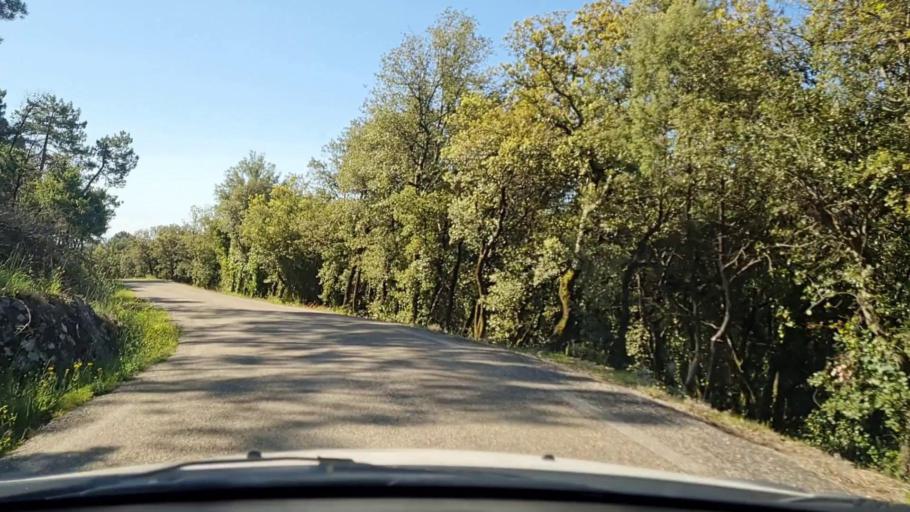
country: FR
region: Languedoc-Roussillon
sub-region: Departement du Gard
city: Branoux-les-Taillades
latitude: 44.1825
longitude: 4.0067
